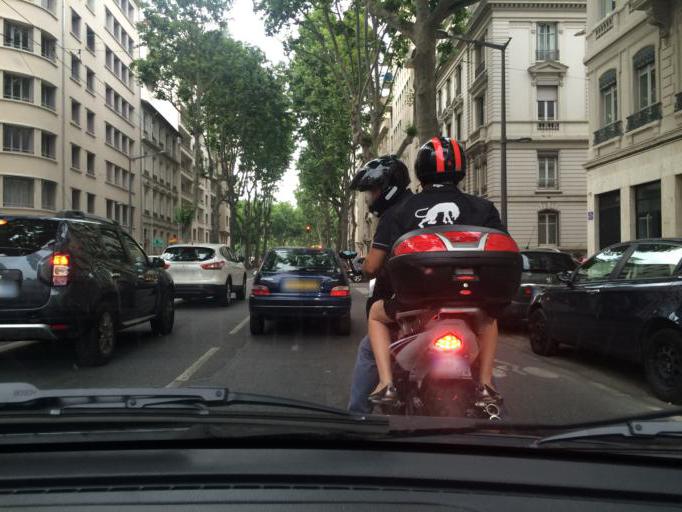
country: FR
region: Rhone-Alpes
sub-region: Departement du Rhone
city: Caluire-et-Cuire
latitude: 45.7730
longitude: 4.8430
